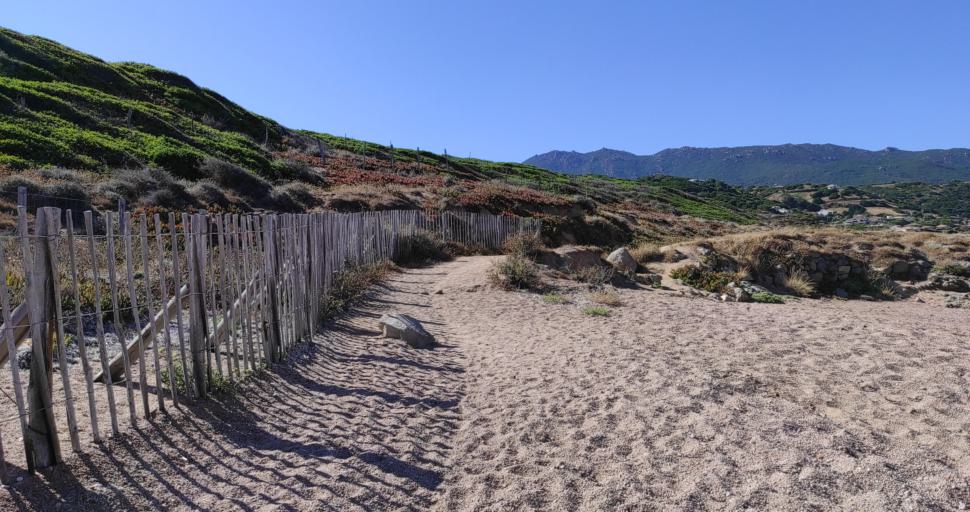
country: FR
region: Corsica
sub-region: Departement de la Corse-du-Sud
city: Alata
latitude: 41.9868
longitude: 8.6704
